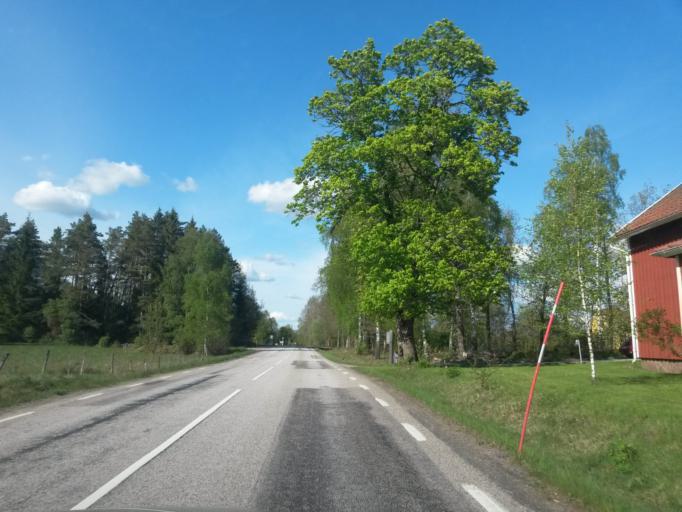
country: SE
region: Vaestra Goetaland
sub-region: Herrljunga Kommun
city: Herrljunga
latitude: 57.9862
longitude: 13.0120
